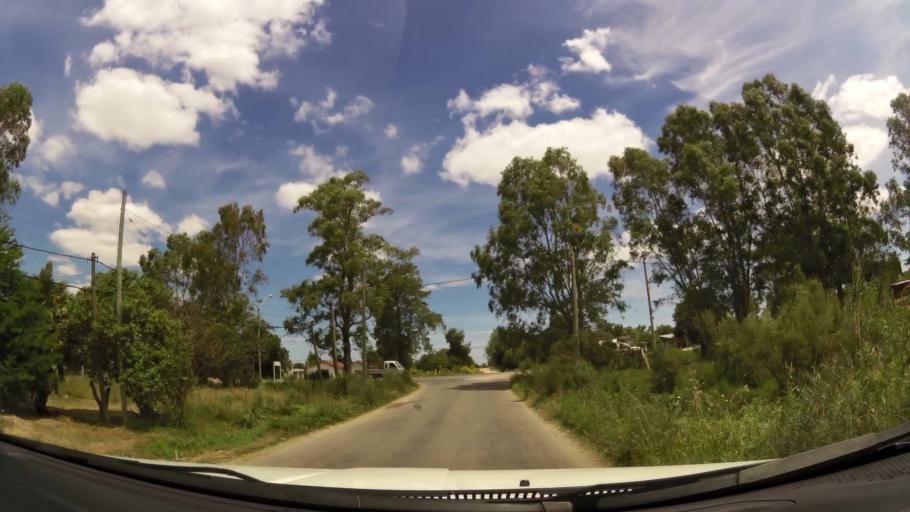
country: UY
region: San Jose
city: Delta del Tigre
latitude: -34.7521
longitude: -56.4150
